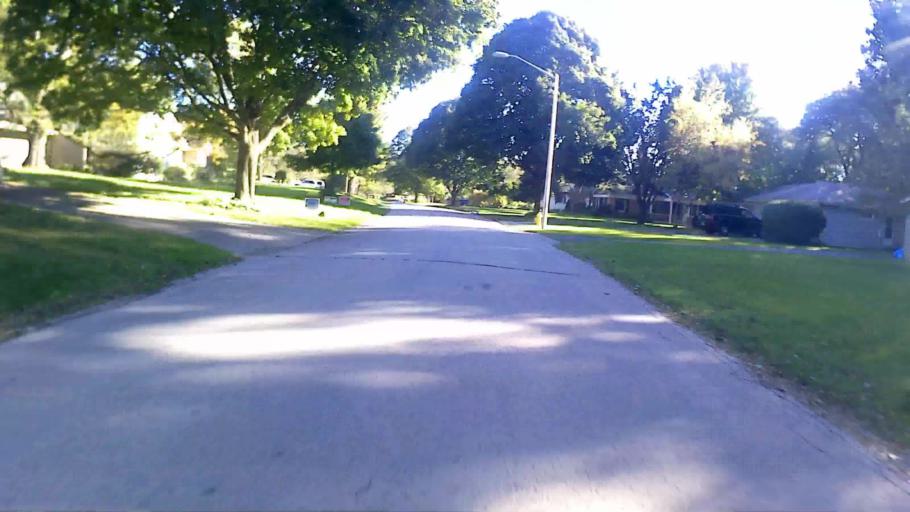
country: US
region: Illinois
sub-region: DuPage County
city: Wheaton
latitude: 41.8566
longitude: -88.1048
